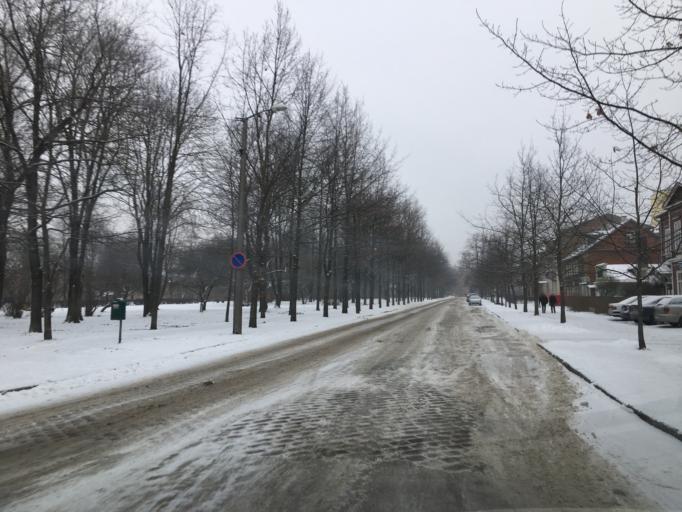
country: EE
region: Tartu
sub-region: Tartu linn
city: Tartu
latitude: 58.3742
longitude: 26.7075
